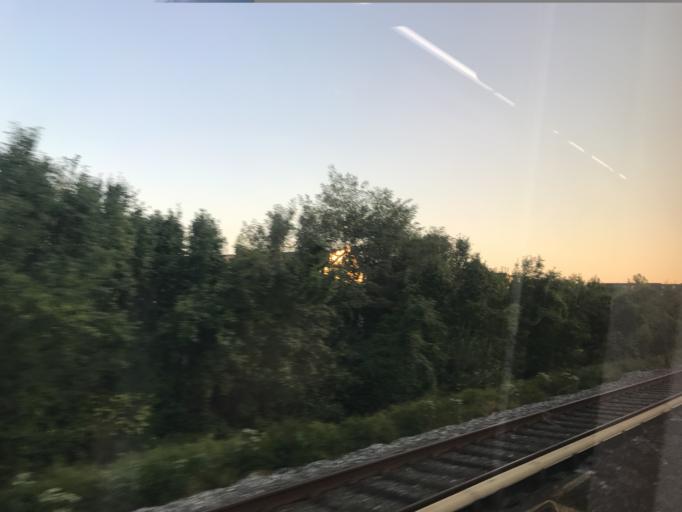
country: US
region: Maryland
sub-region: Prince George's County
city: Berwyn Heights
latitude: 39.0054
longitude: -76.9163
